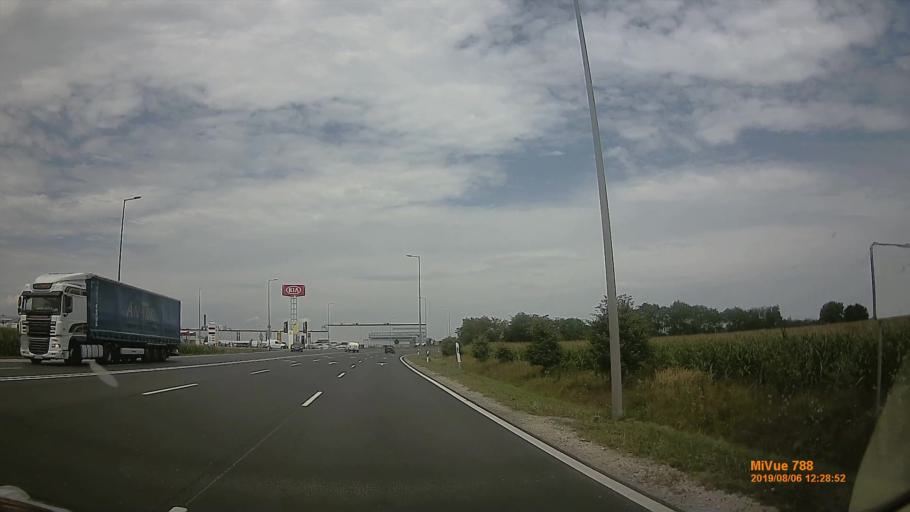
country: HU
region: Vas
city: Szombathely
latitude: 47.2267
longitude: 16.6566
